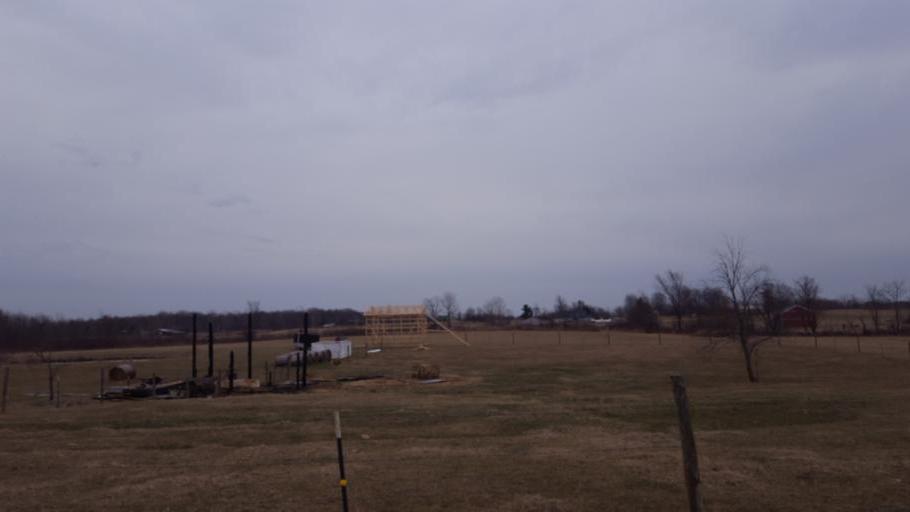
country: US
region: Ohio
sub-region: Morrow County
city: Mount Gilead
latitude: 40.6272
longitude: -82.7914
